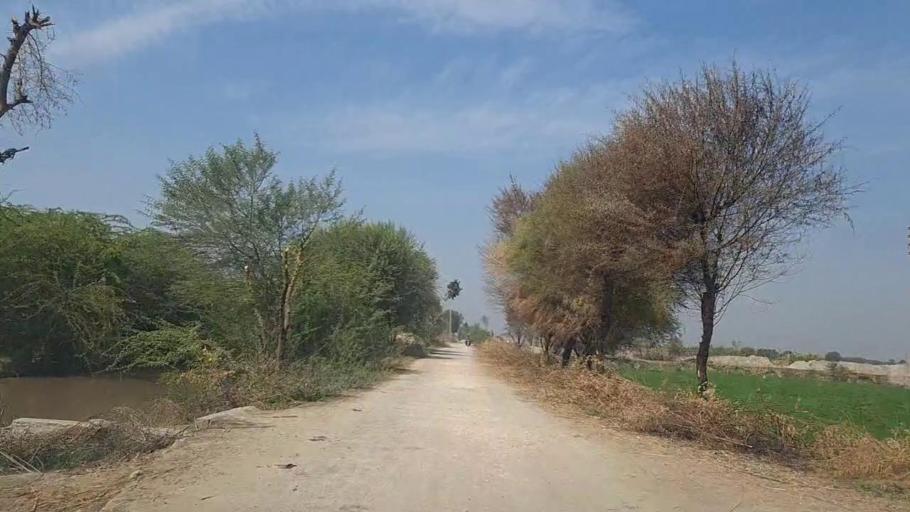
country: PK
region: Sindh
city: Mirpur Khas
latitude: 25.4855
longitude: 68.9262
